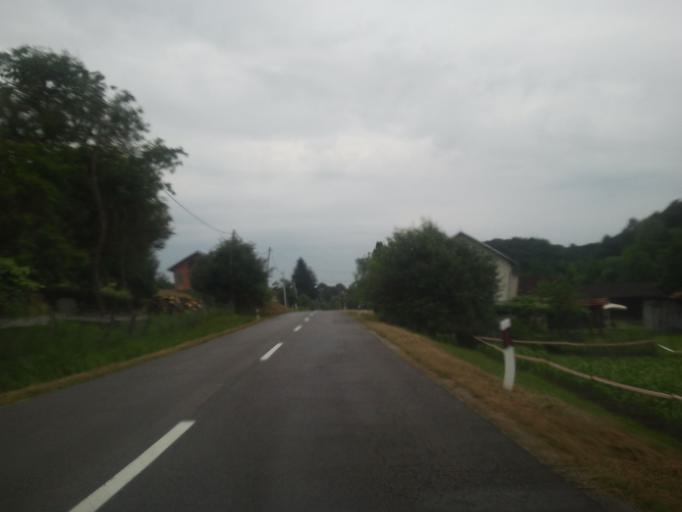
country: HR
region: Karlovacka
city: Vojnic
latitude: 45.3275
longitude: 15.7106
